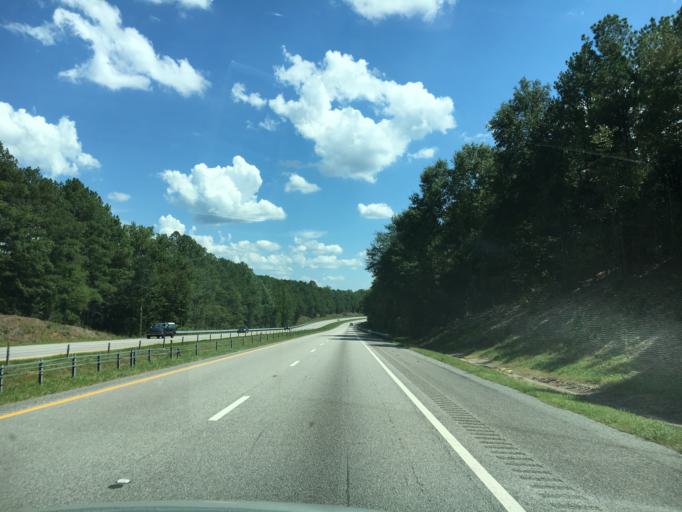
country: US
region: South Carolina
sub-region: Laurens County
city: Watts Mills
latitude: 34.6071
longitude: -81.8946
